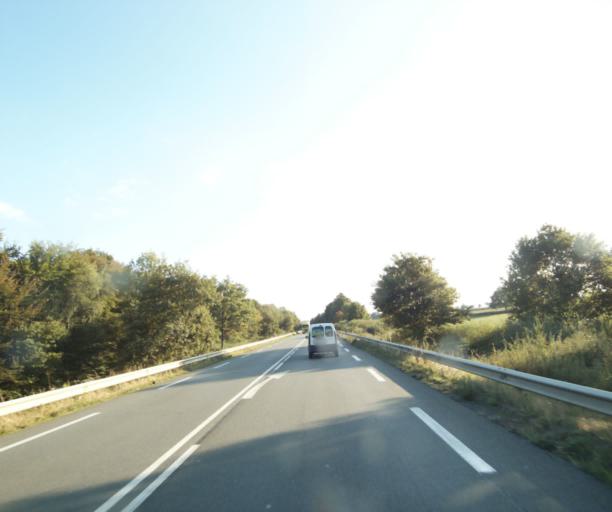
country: FR
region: Bourgogne
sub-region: Departement de Saone-et-Loire
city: Palinges
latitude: 46.5318
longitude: 4.1677
